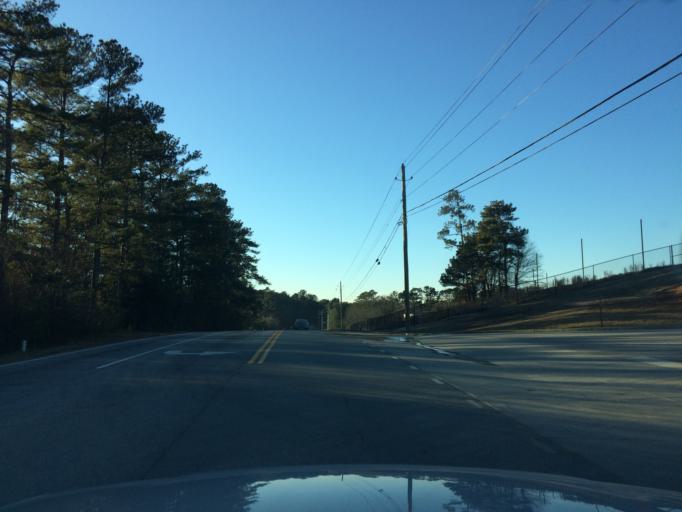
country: US
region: Georgia
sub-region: Barrow County
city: Winder
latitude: 33.9679
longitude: -83.7763
